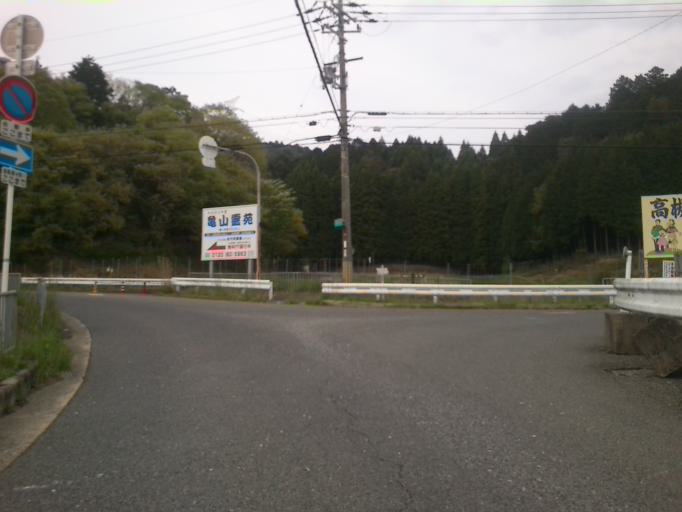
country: JP
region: Kyoto
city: Kameoka
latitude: 34.9614
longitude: 135.5906
